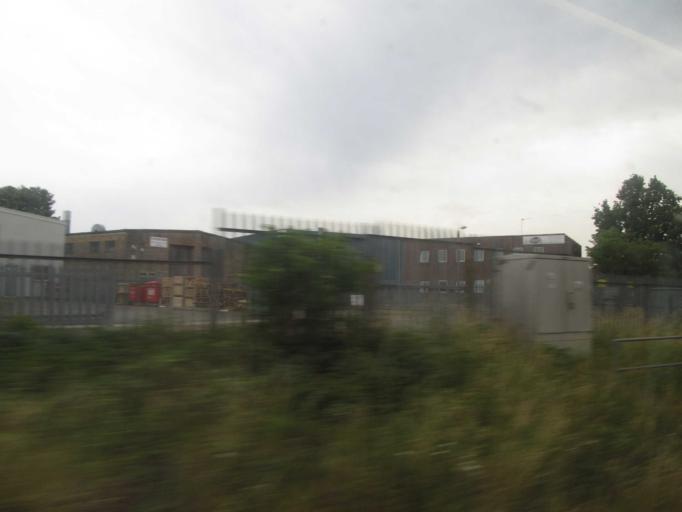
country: GB
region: England
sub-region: Bedford
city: Bedford
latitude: 52.1208
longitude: -0.4785
